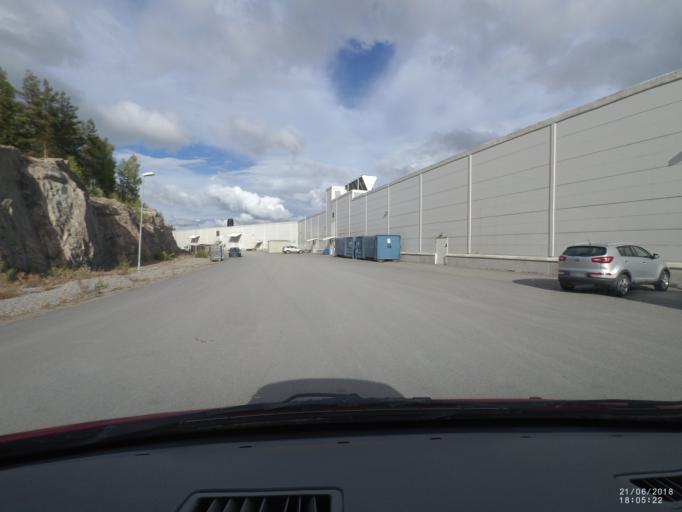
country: SE
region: Soedermanland
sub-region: Nykopings Kommun
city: Nykoping
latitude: 58.7726
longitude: 17.0180
